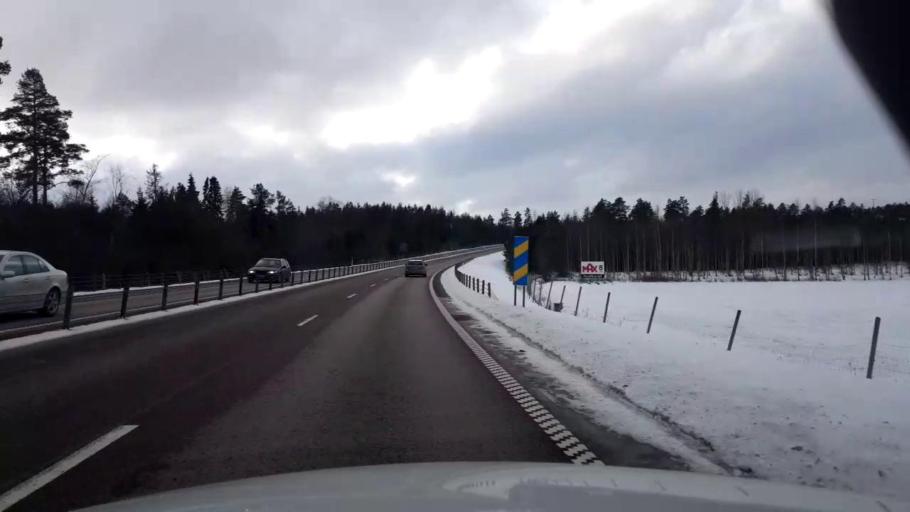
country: SE
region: Gaevleborg
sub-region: Hudiksvalls Kommun
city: Hudiksvall
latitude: 61.7974
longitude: 17.1696
